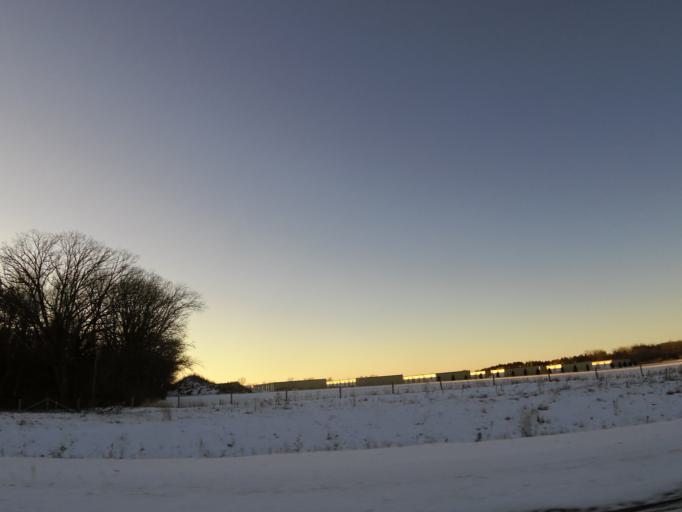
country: US
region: Minnesota
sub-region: Washington County
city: Stillwater
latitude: 45.0682
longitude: -92.7816
